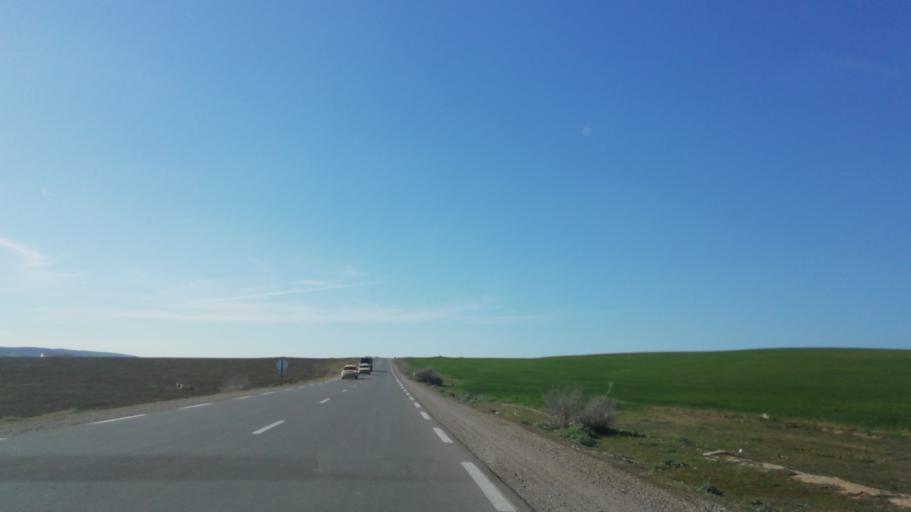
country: DZ
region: Mascara
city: Oued el Abtal
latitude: 35.4467
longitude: 0.8185
